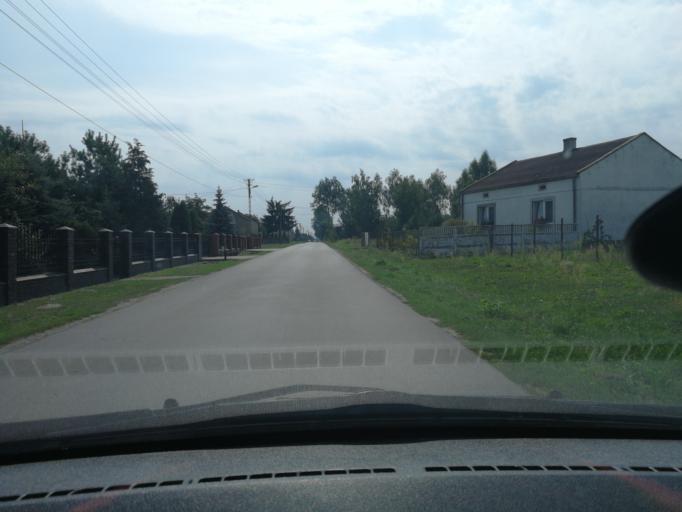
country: PL
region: Lodz Voivodeship
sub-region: Powiat skierniewicki
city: Makow
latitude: 52.0102
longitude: 20.0678
